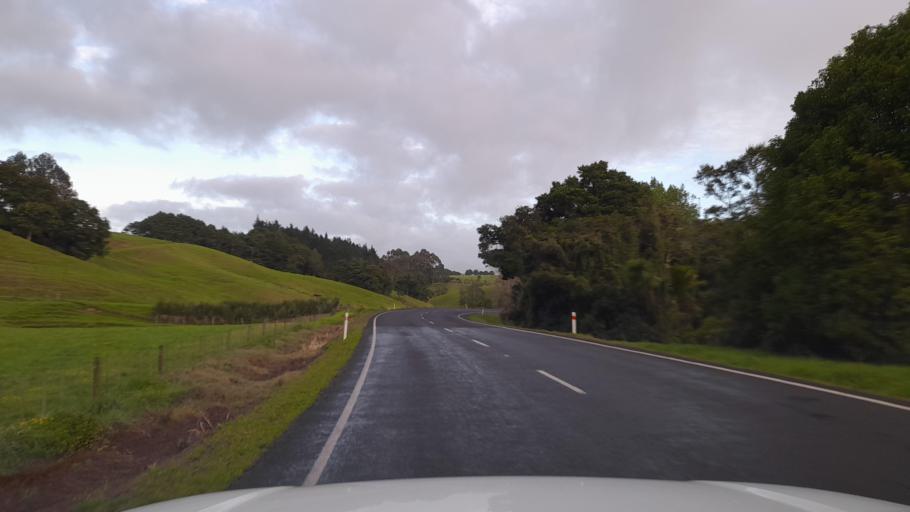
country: NZ
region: Northland
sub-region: Kaipara District
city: Dargaville
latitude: -35.6989
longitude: 173.9126
